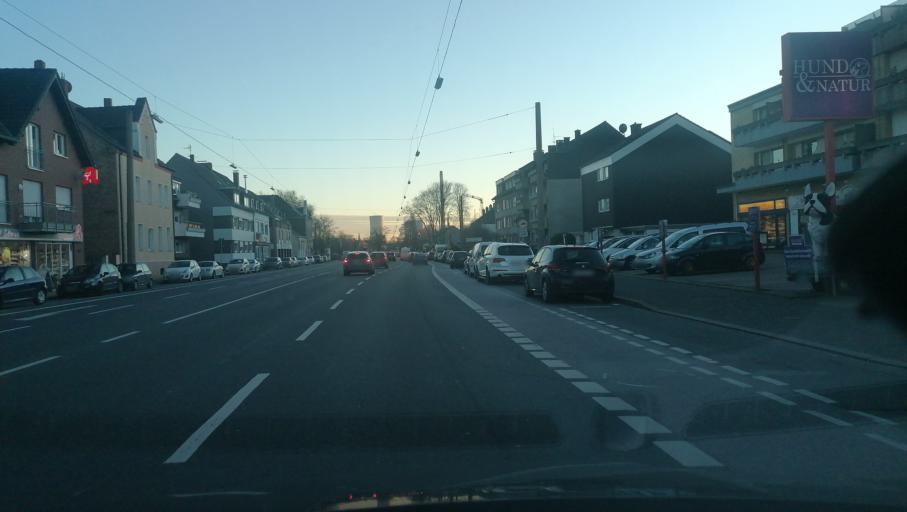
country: DE
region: North Rhine-Westphalia
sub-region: Regierungsbezirk Munster
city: Recklinghausen
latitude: 51.5744
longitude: 7.1850
